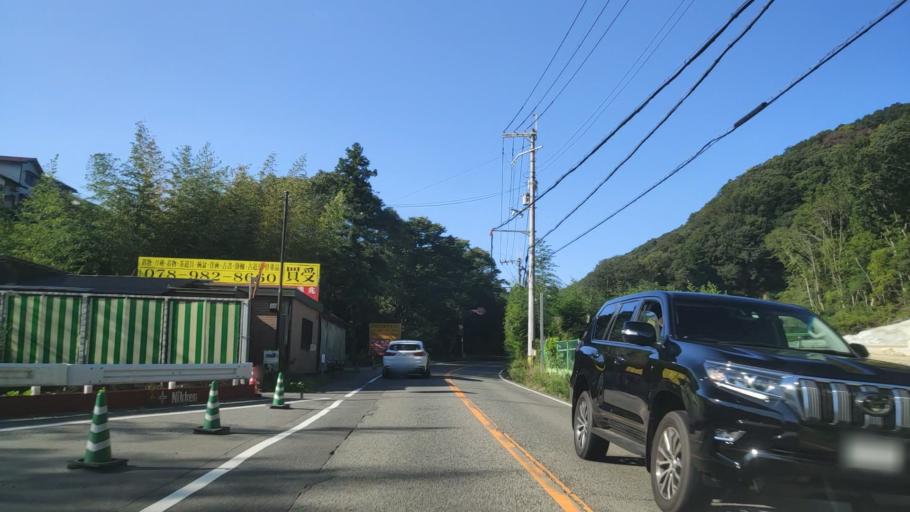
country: JP
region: Hyogo
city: Sandacho
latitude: 34.7945
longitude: 135.2155
